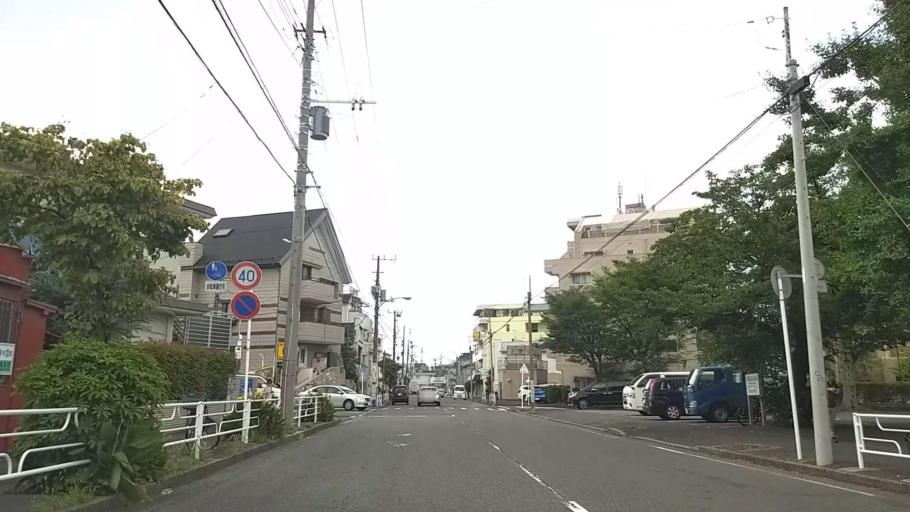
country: JP
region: Kanagawa
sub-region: Kawasaki-shi
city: Kawasaki
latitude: 35.5044
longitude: 139.6893
